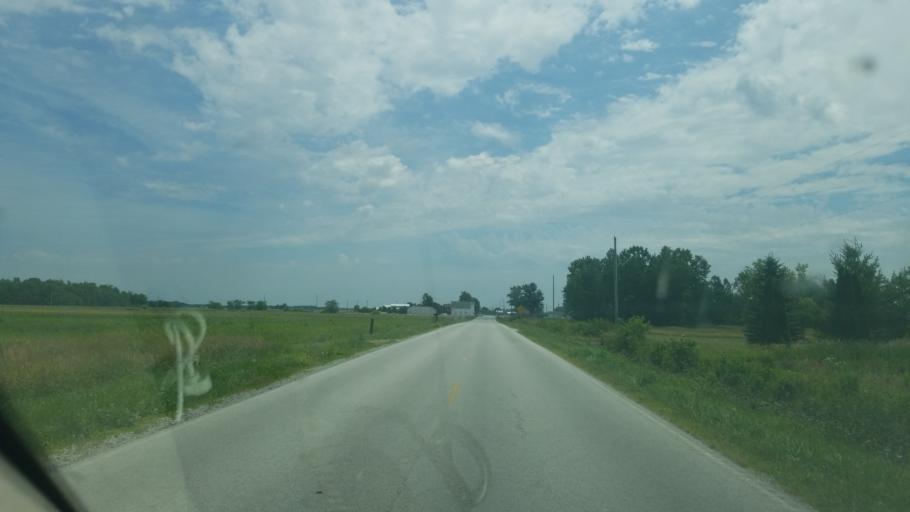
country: US
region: Ohio
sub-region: Wood County
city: Bowling Green
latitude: 41.2967
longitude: -83.5978
